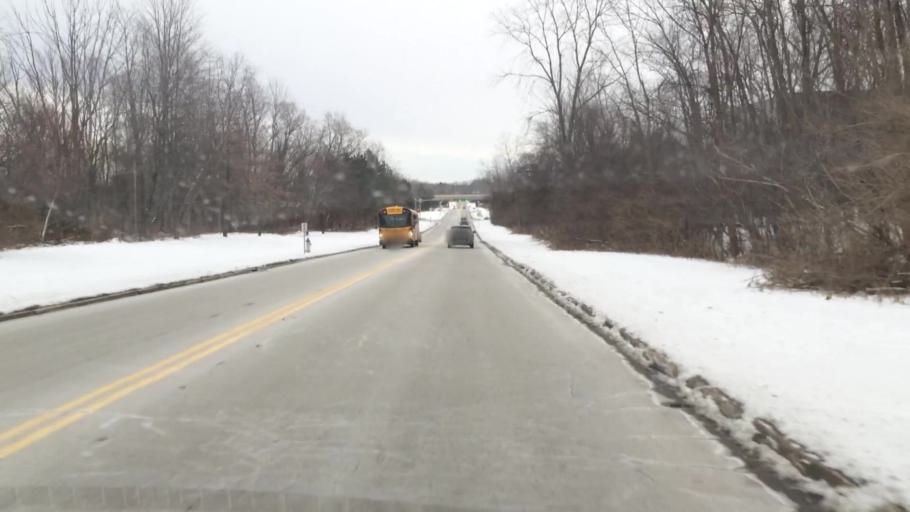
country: US
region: Ohio
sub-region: Cuyahoga County
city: Beachwood
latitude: 41.4736
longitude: -81.4945
